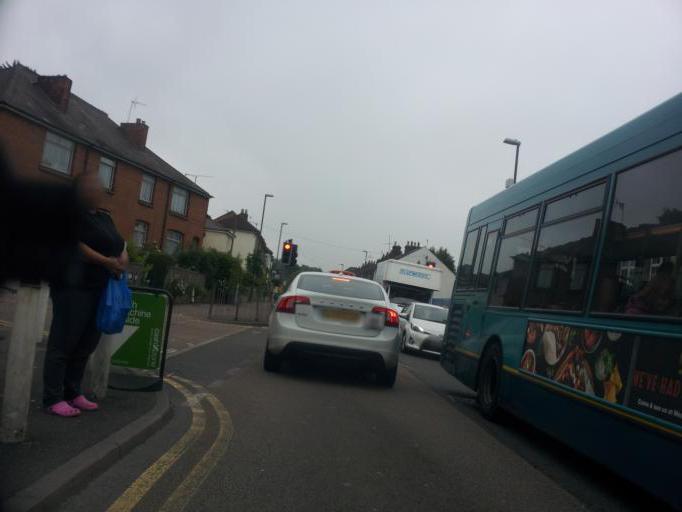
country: GB
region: England
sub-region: Kent
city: Chatham
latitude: 51.3725
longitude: 0.5436
